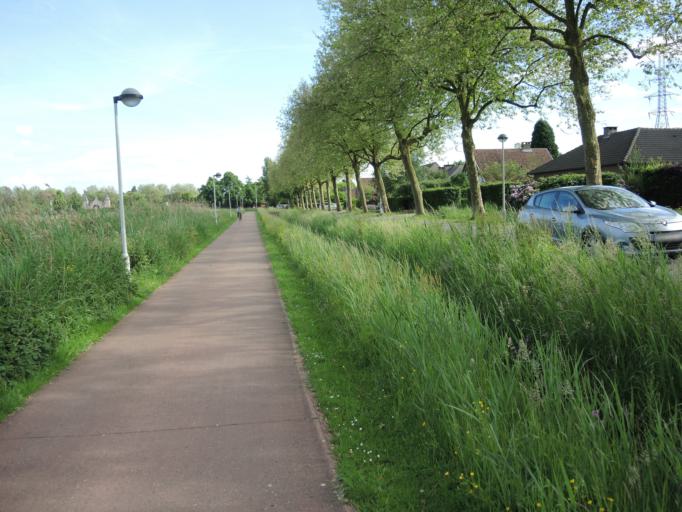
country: BE
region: Flanders
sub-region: Provincie Antwerpen
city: Kapellen
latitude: 51.2906
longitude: 4.4246
